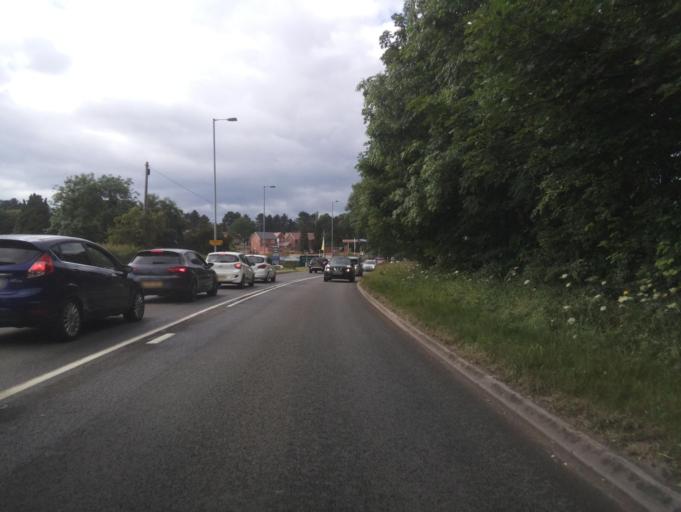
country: GB
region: England
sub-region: Dudley
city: Kingswinford
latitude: 52.5272
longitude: -2.1787
